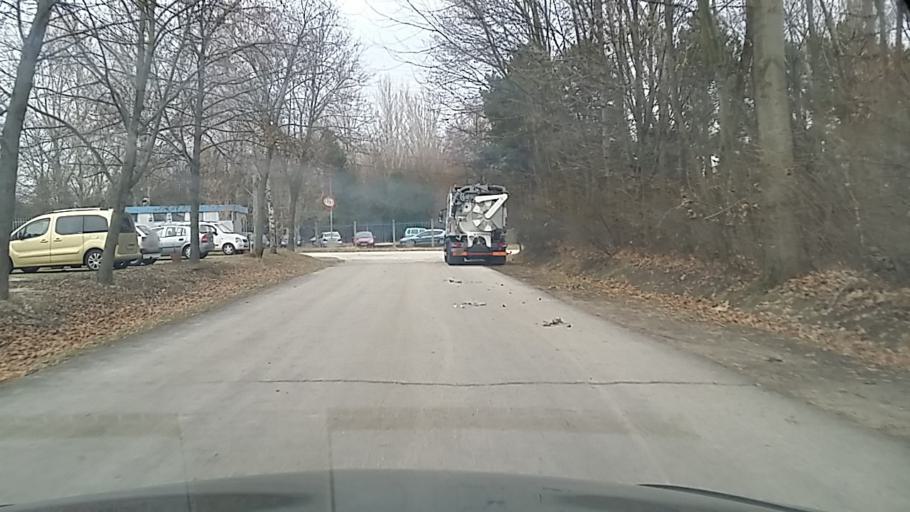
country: HU
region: Fejer
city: Szekesfehervar
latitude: 47.1651
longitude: 18.4251
